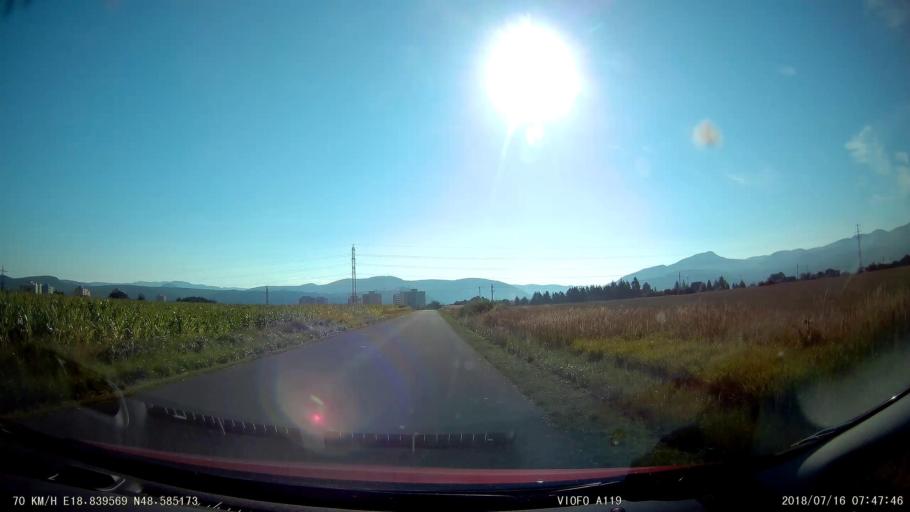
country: SK
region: Banskobystricky
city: Ziar nad Hronom
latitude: 48.5853
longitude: 18.8394
